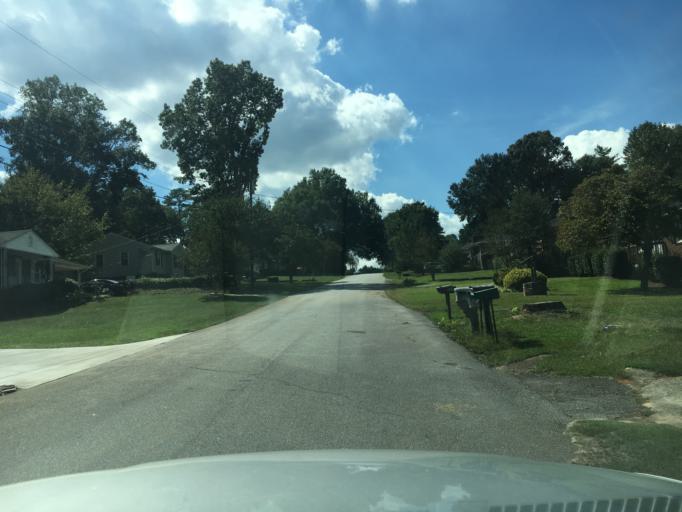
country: US
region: South Carolina
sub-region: Spartanburg County
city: Lyman
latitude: 34.9317
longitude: -82.1227
